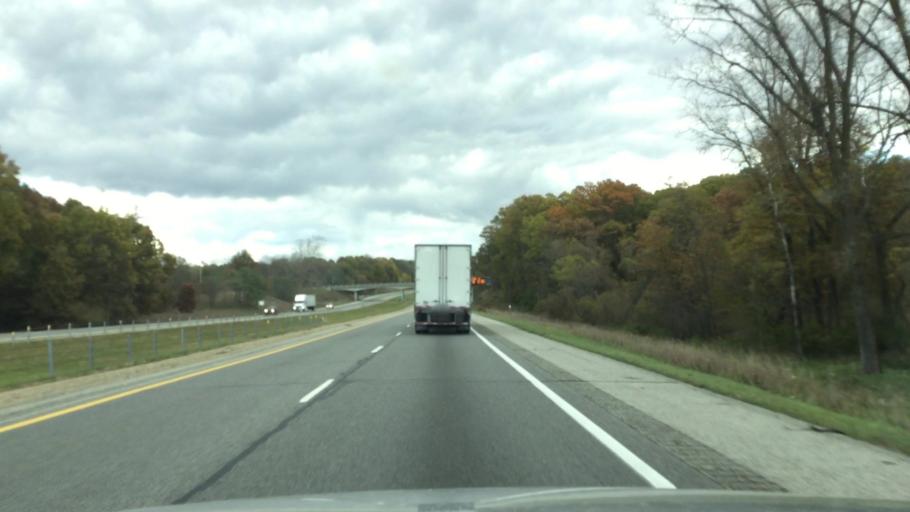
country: US
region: Michigan
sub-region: Van Buren County
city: Mattawan
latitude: 42.2338
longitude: -85.7107
